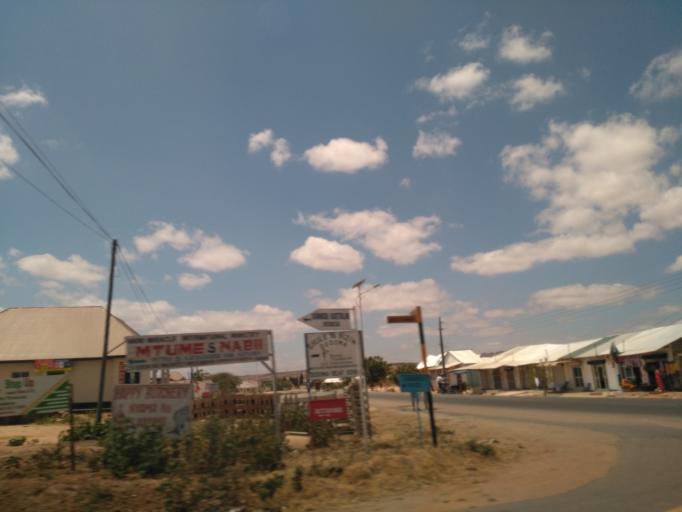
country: TZ
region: Dodoma
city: Kisasa
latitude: -6.1665
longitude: 35.7899
